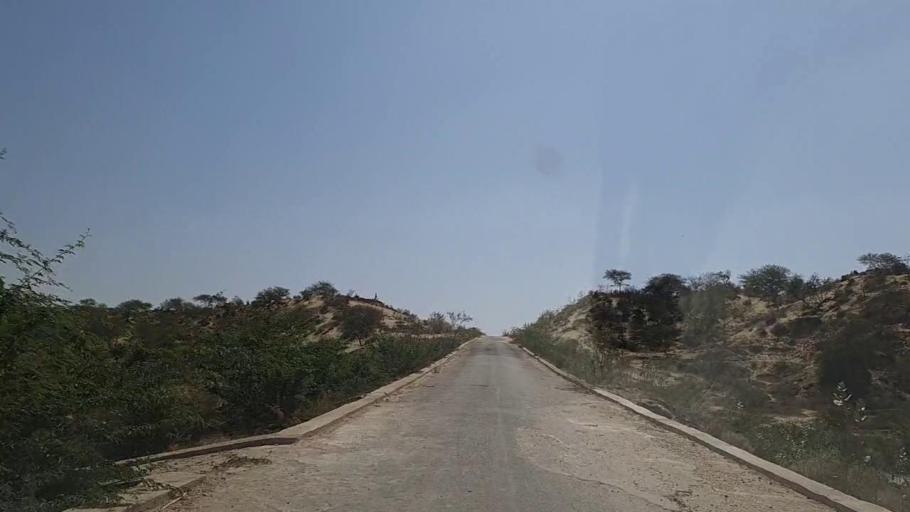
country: PK
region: Sindh
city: Diplo
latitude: 24.5068
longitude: 69.4239
